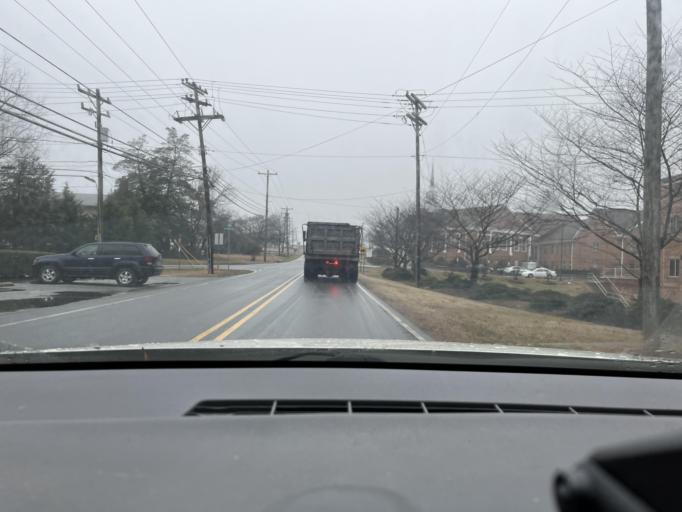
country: US
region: North Carolina
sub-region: Guilford County
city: Pleasant Garden
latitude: 35.9620
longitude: -79.7590
